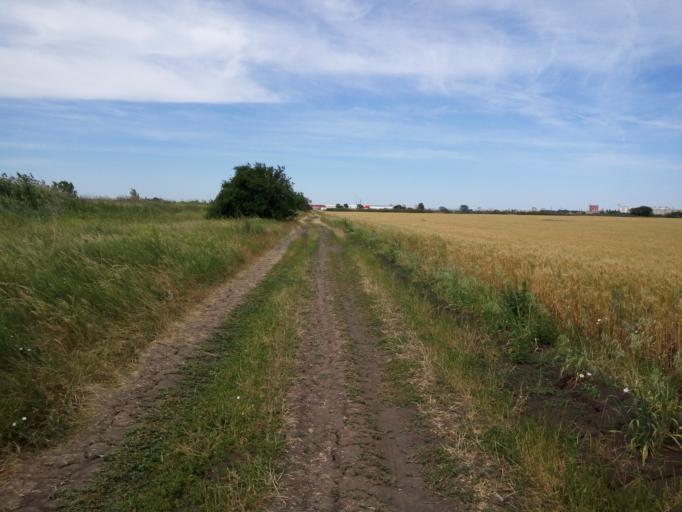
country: RU
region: Rostov
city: Bataysk
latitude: 47.1167
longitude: 39.7229
